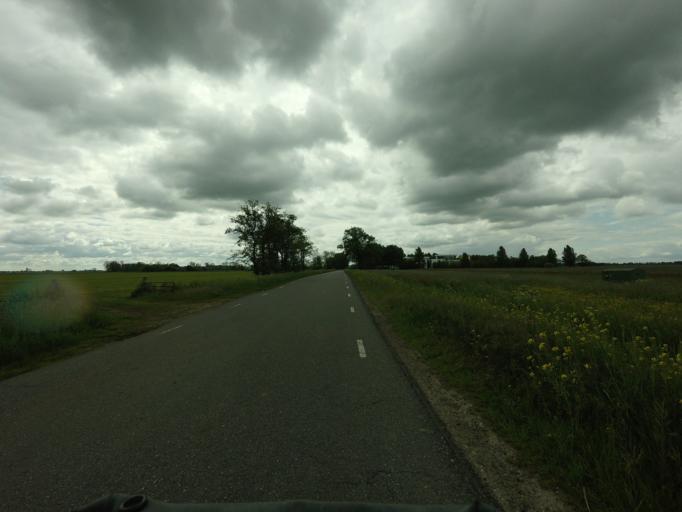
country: NL
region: Utrecht
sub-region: Gemeente Lopik
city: Lopik
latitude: 51.9381
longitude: 4.9359
